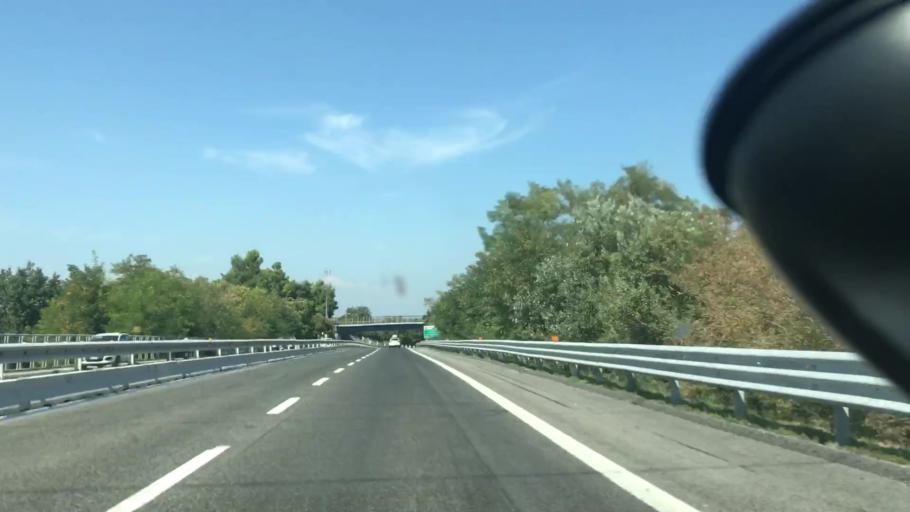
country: IT
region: Abruzzo
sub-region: Provincia di Chieti
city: Vasto
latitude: 42.1354
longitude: 14.6646
